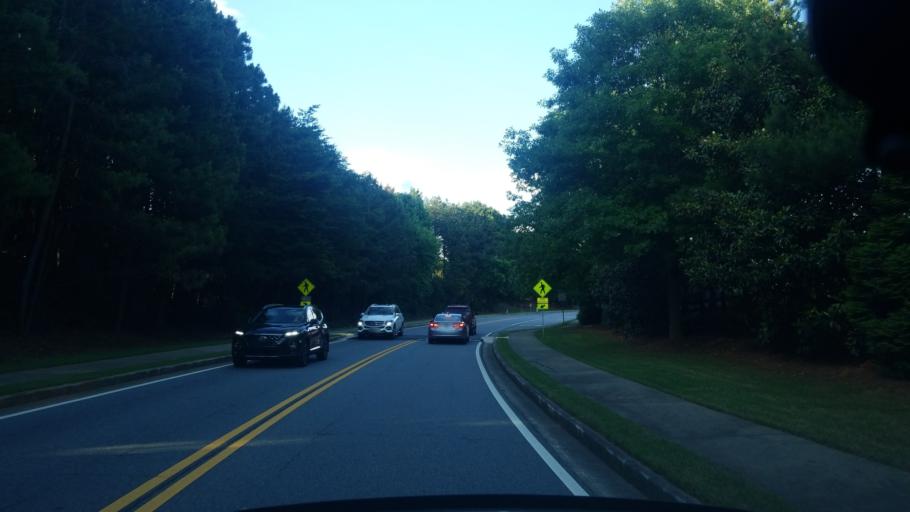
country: US
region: Georgia
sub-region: Fulton County
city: Johns Creek
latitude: 34.0892
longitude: -84.1551
